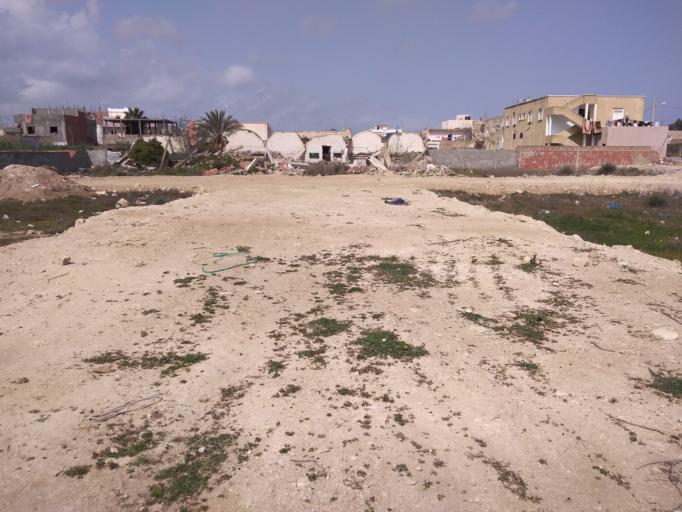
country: TN
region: Ariana
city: Ariana
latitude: 36.9480
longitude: 10.1729
